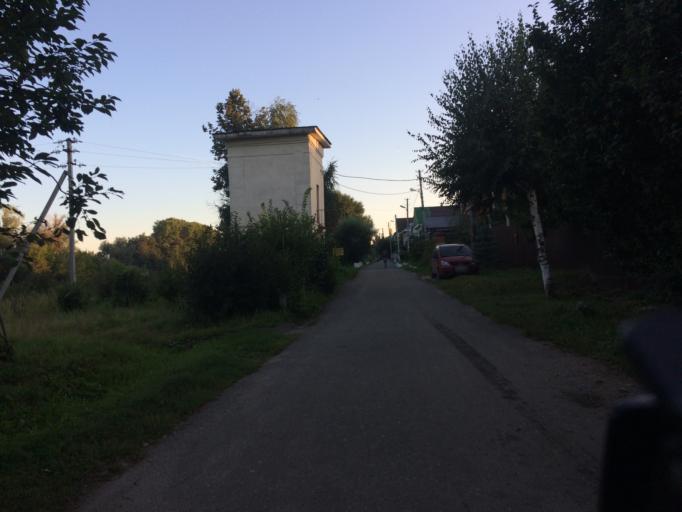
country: RU
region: Mariy-El
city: Yoshkar-Ola
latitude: 56.6424
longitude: 47.9069
